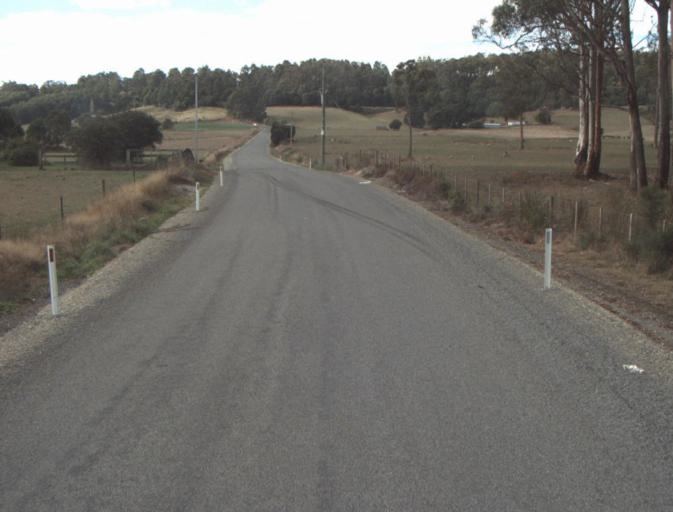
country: AU
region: Tasmania
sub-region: Launceston
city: Mayfield
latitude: -41.2073
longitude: 147.1880
